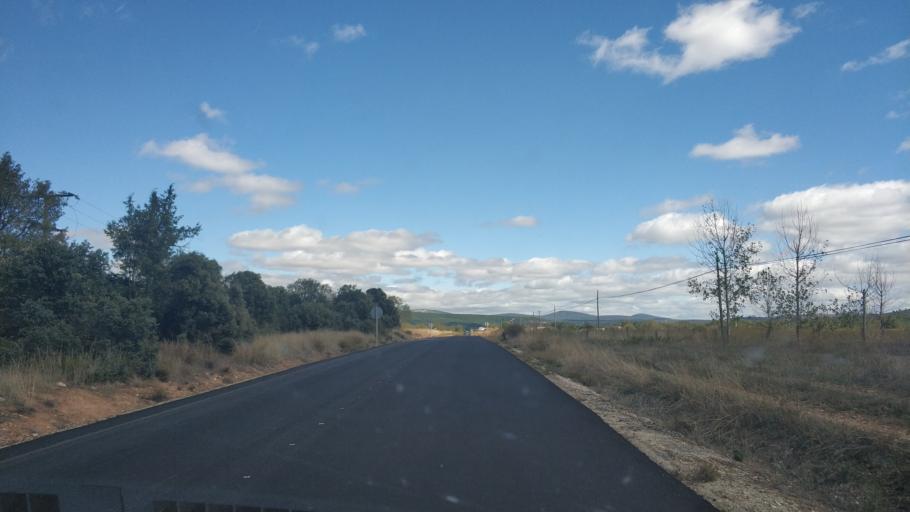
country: ES
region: Castille and Leon
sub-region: Provincia de Burgos
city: Puentedura
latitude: 42.0386
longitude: -3.5962
